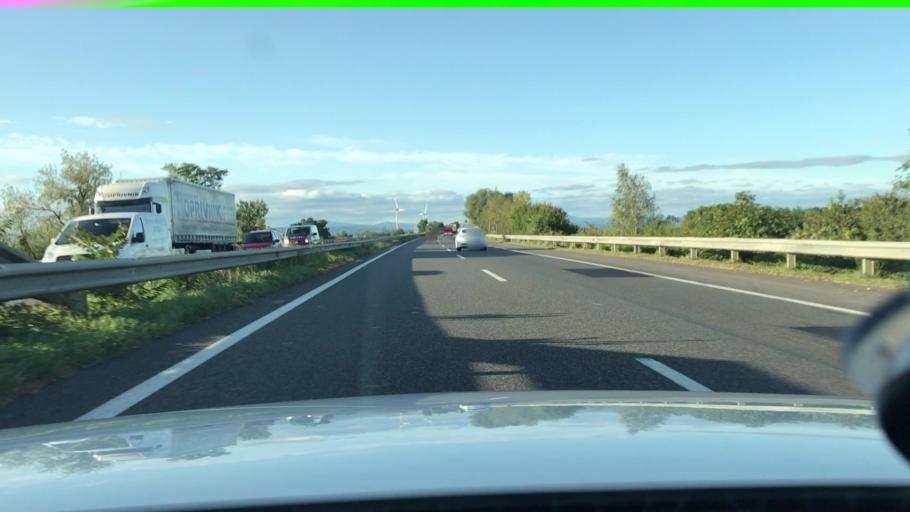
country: AT
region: Lower Austria
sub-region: Sankt Polten Stadt
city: Sankt Poelten
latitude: 48.2253
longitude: 15.6794
